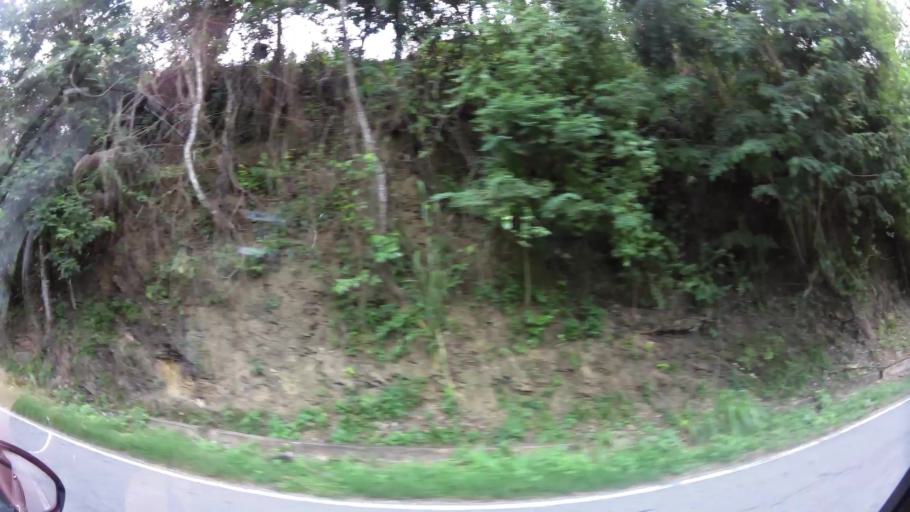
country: TT
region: Diego Martin
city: Petit Valley
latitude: 10.7324
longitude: -61.4917
